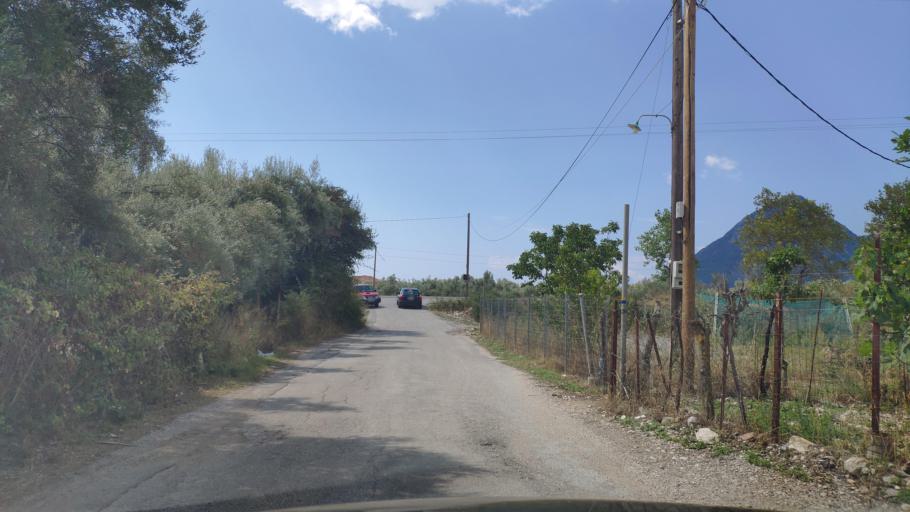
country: GR
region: West Greece
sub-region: Nomos Aitolias kai Akarnanias
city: Kandila
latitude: 38.6771
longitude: 20.9824
